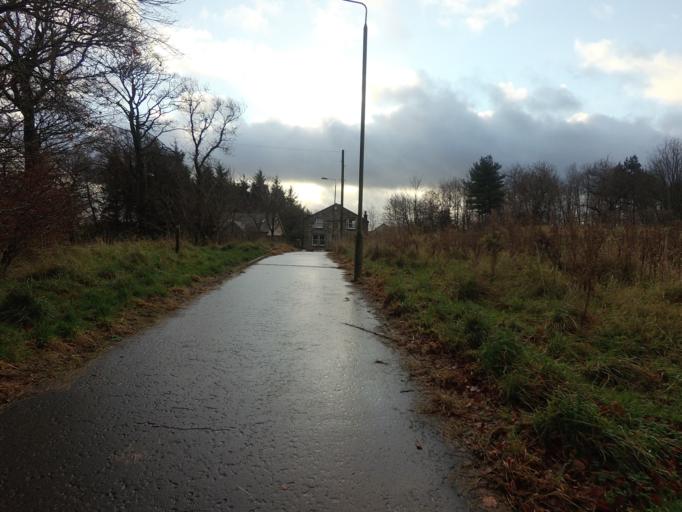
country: GB
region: Scotland
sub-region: West Lothian
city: West Calder
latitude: 55.8874
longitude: -3.5592
